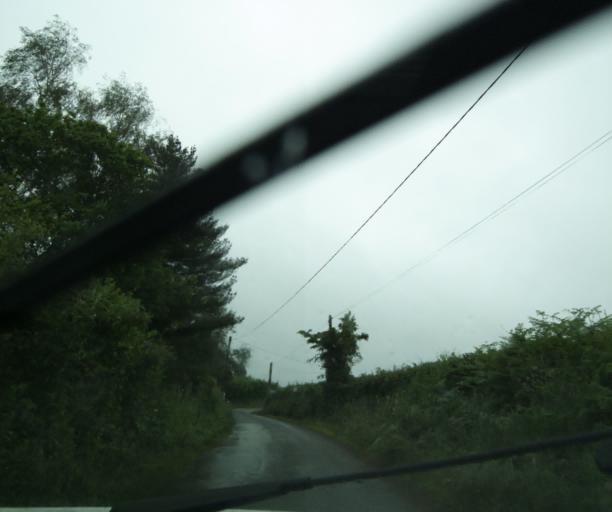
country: FR
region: Bourgogne
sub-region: Departement de Saone-et-Loire
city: Ciry-le-Noble
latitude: 46.5507
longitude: 4.3139
